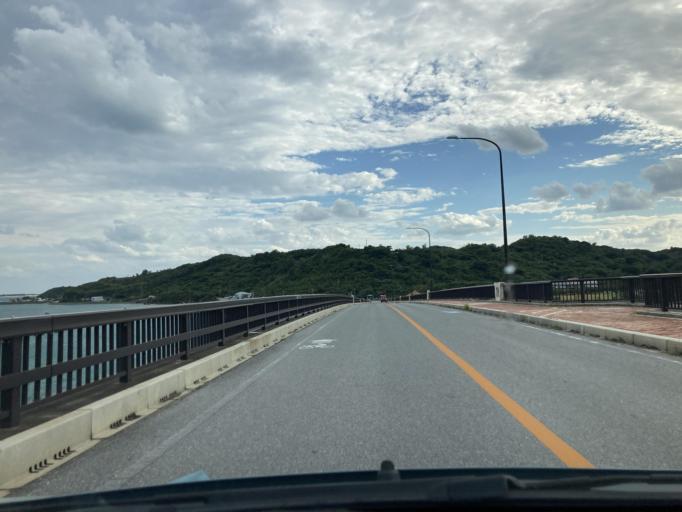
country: JP
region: Okinawa
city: Katsuren-haebaru
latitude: 26.3322
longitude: 127.9561
